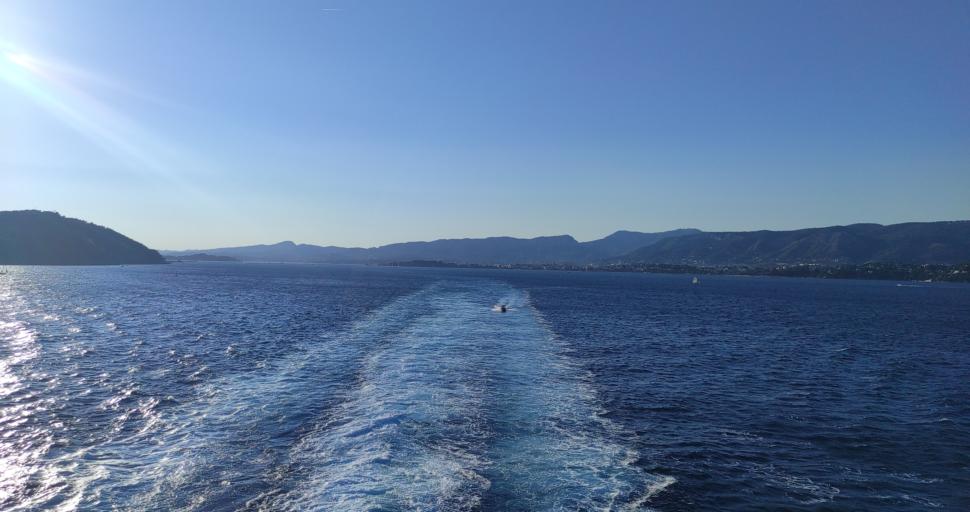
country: FR
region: Provence-Alpes-Cote d'Azur
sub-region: Departement du Var
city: Saint-Mandrier-sur-Mer
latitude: 43.0721
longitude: 5.9687
